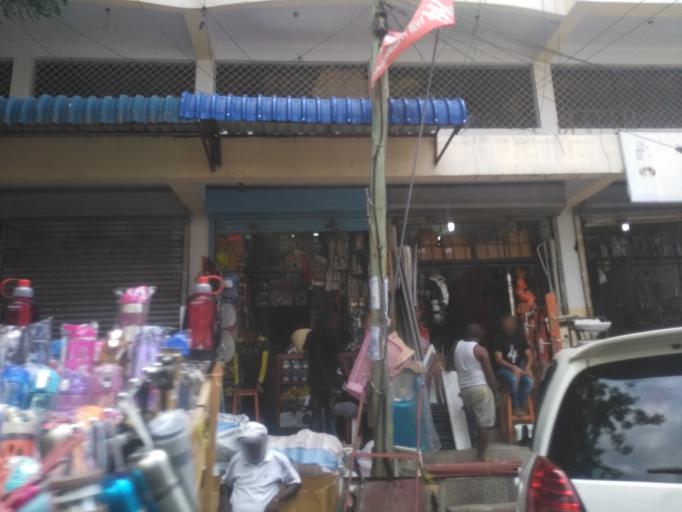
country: TZ
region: Dar es Salaam
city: Dar es Salaam
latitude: -6.8214
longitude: 39.2758
